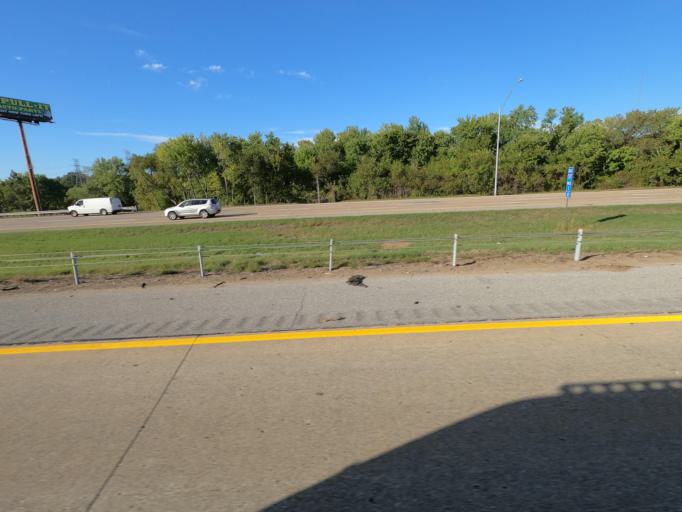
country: US
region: Tennessee
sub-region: Shelby County
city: Memphis
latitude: 35.1925
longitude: -89.9981
